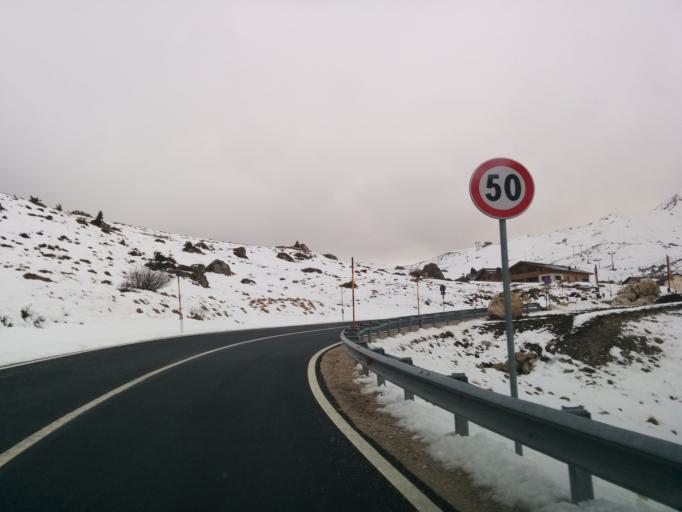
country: IT
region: Trentino-Alto Adige
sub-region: Provincia di Trento
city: Canazei
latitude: 46.5102
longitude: 11.7596
